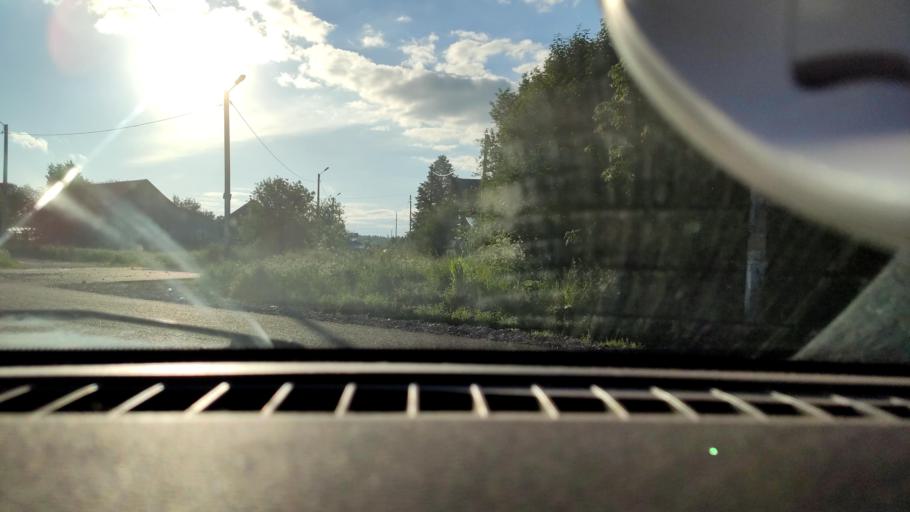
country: RU
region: Perm
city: Novyye Lyady
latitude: 58.0567
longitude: 56.6017
